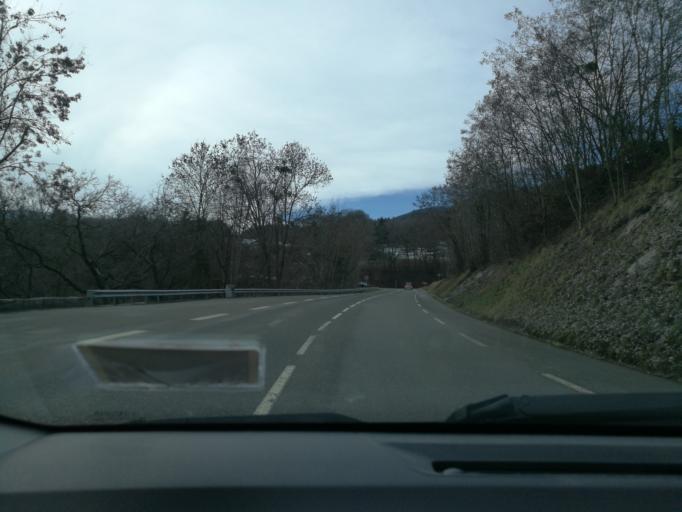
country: FR
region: Rhone-Alpes
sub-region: Departement de la Haute-Savoie
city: Sallanches
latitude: 45.9270
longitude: 6.6331
